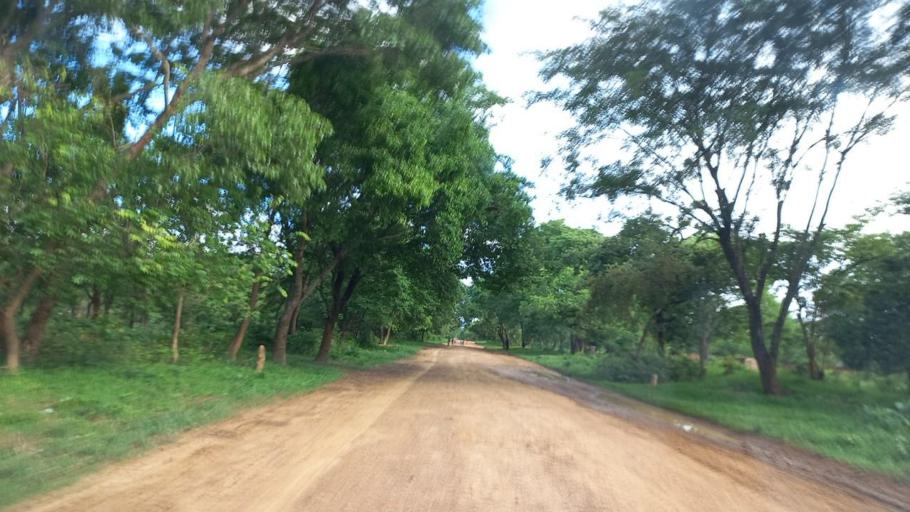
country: ZM
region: North-Western
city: Kabompo
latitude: -13.3732
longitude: 24.2979
